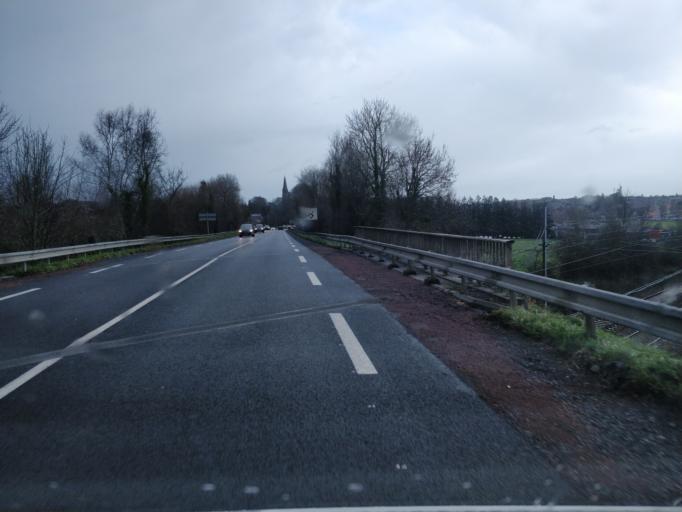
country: FR
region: Lower Normandy
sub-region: Departement du Calvados
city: Bayeux
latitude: 49.2678
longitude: -0.7092
